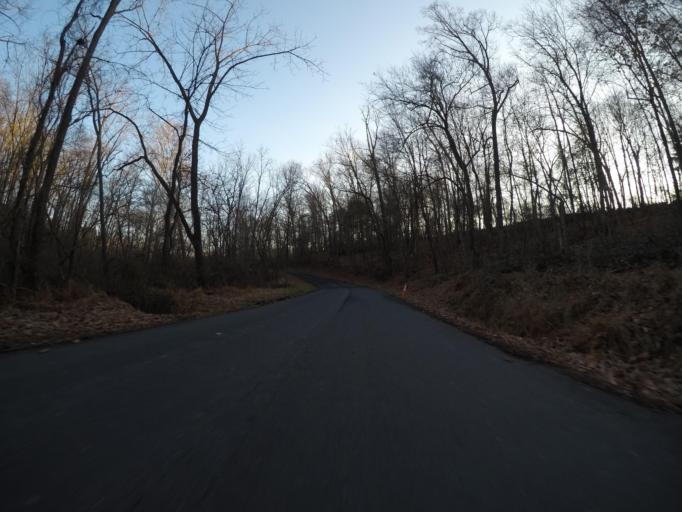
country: US
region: Maryland
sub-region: Carroll County
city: Hampstead
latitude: 39.5779
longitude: -76.8135
